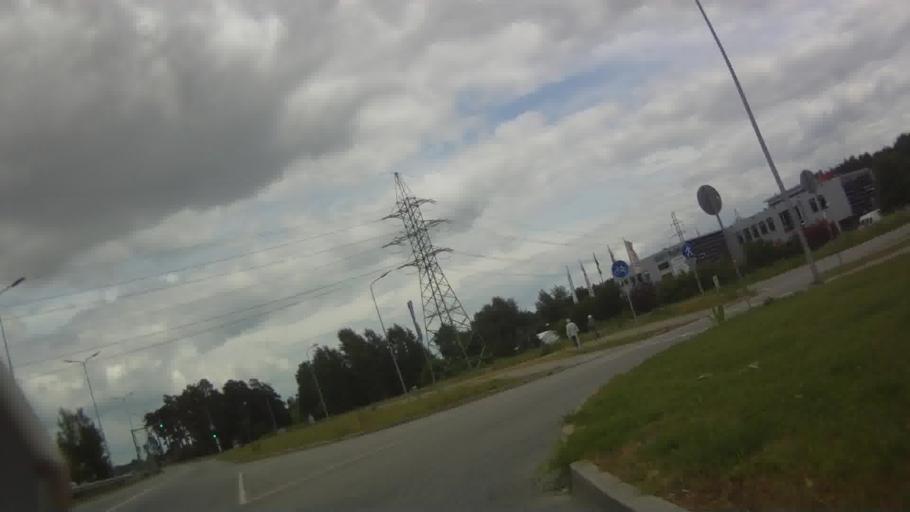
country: LV
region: Stopini
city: Ulbroka
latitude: 56.9433
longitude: 24.2303
